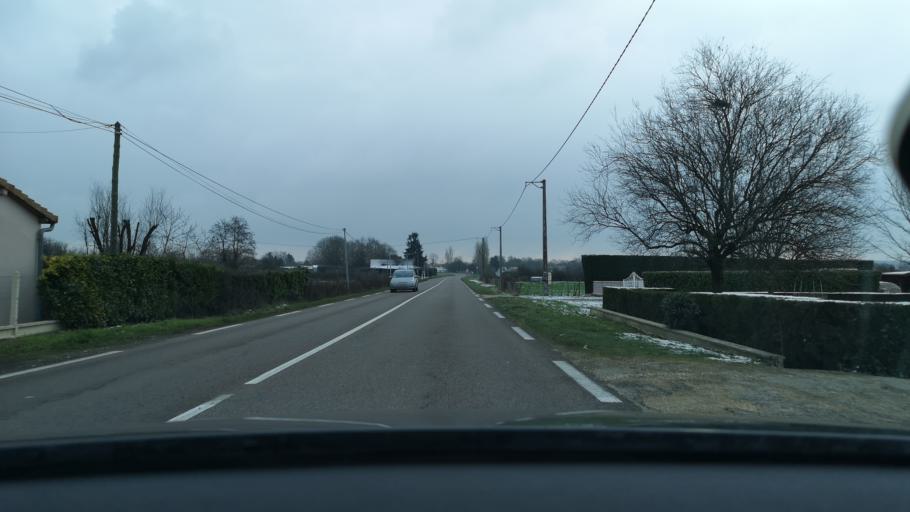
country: FR
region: Bourgogne
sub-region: Departement de Saone-et-Loire
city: Ouroux-sur-Saone
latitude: 46.7620
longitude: 4.9901
